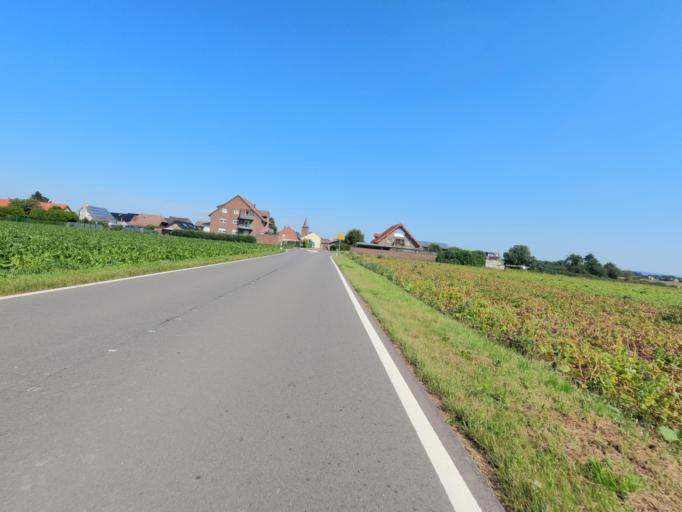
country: DE
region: North Rhine-Westphalia
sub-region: Regierungsbezirk Koln
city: Linnich
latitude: 50.9623
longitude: 6.2727
